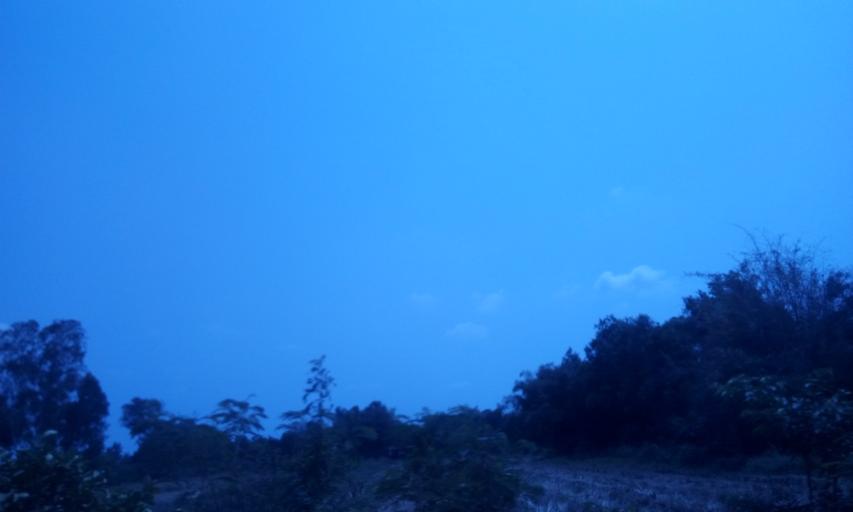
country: TH
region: Chachoengsao
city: Bang Nam Priao
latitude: 13.9098
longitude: 100.9736
